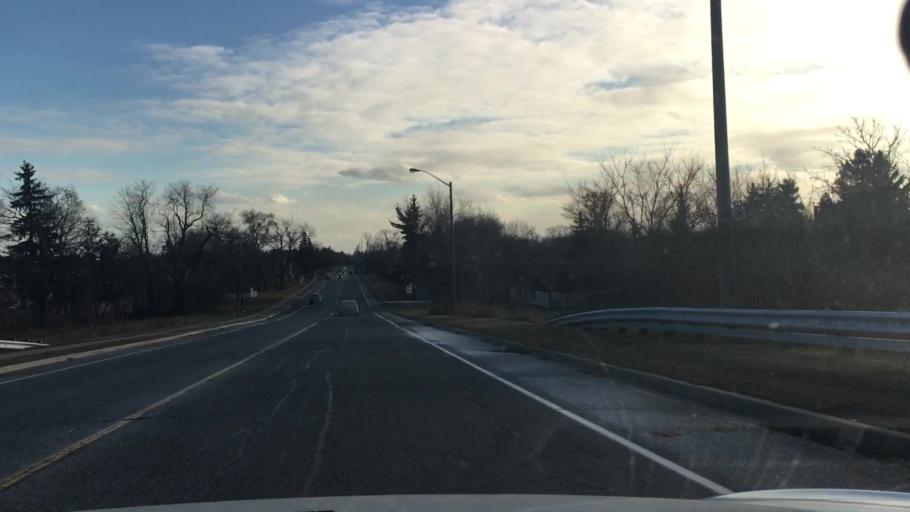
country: CA
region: Ontario
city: Scarborough
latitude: 43.7967
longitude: -79.1869
